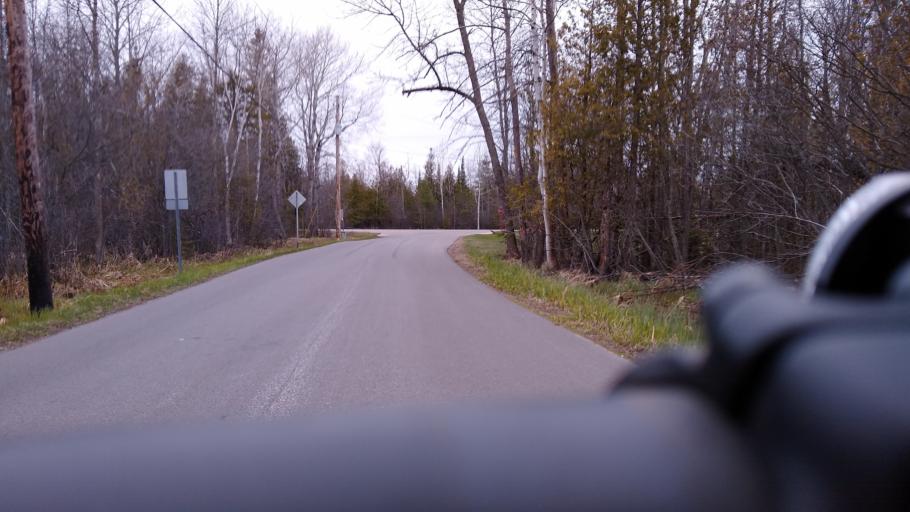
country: US
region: Michigan
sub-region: Delta County
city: Escanaba
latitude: 45.7012
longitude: -87.1001
